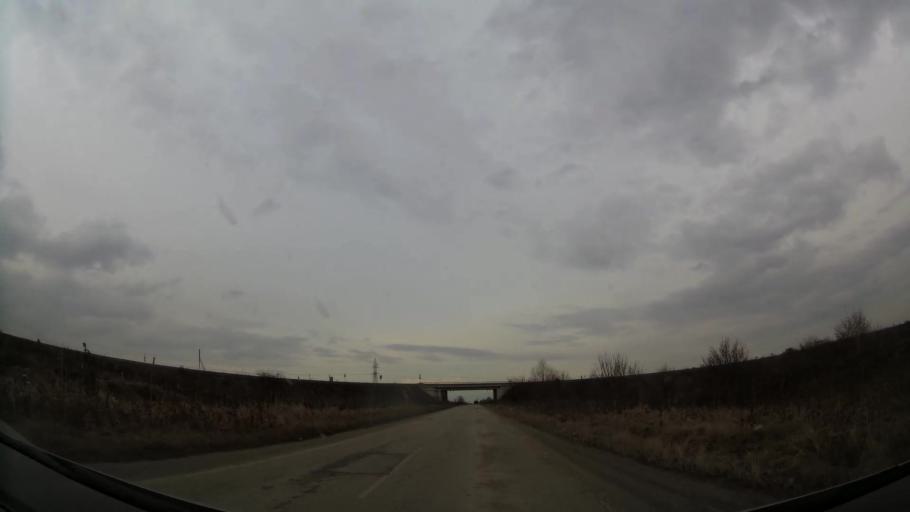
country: BG
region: Sofiya
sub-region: Obshtina Bozhurishte
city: Bozhurishte
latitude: 42.7080
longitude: 23.2188
